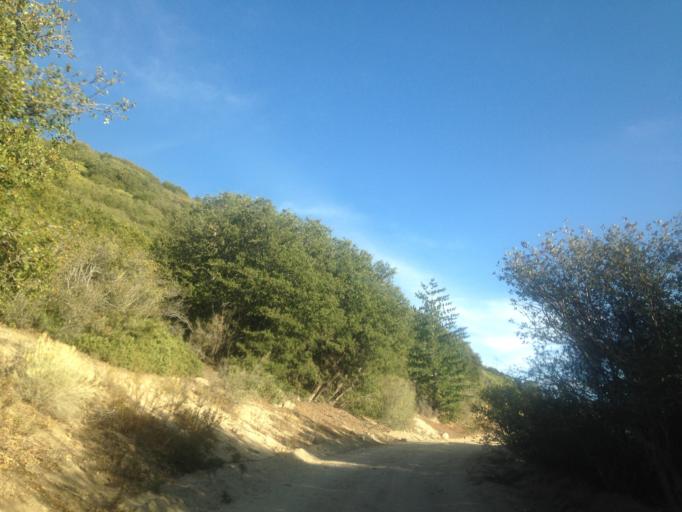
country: US
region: California
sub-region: San Bernardino County
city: Yucaipa
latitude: 34.1370
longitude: -117.0038
